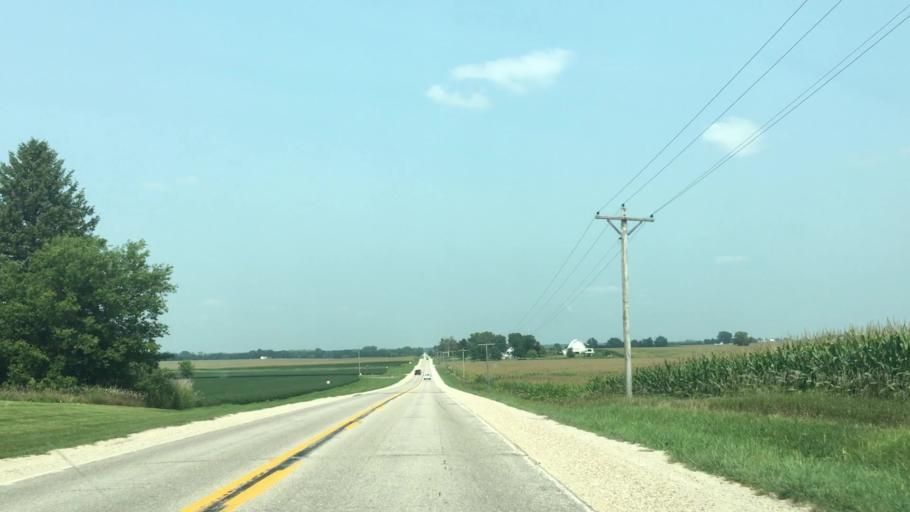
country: US
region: Iowa
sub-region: Benton County
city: Urbana
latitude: 42.3386
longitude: -91.8894
